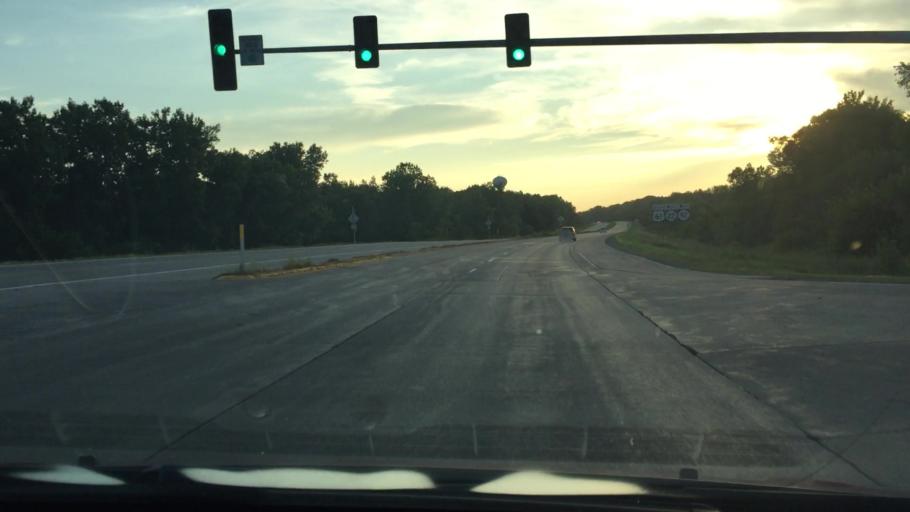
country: US
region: Iowa
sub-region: Muscatine County
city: Muscatine
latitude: 41.4519
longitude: -91.0424
